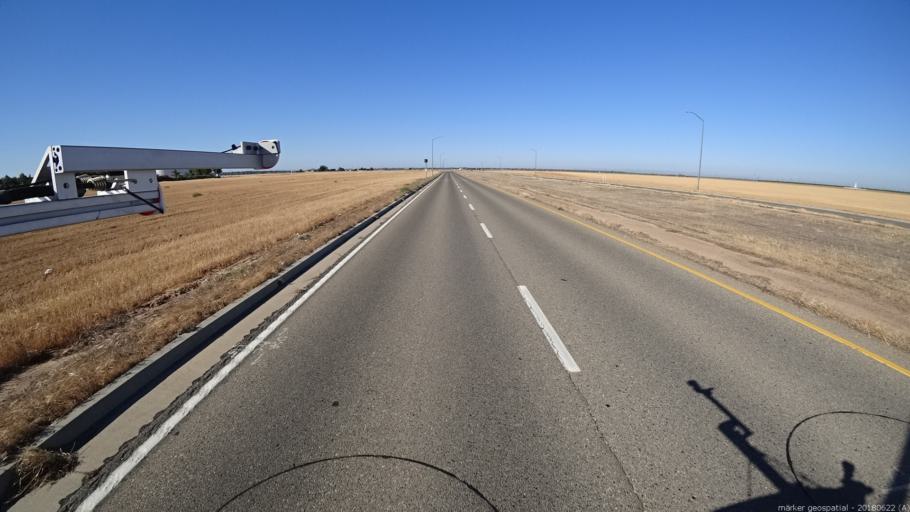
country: US
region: California
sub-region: Fresno County
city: Clovis
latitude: 36.8863
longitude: -119.8051
